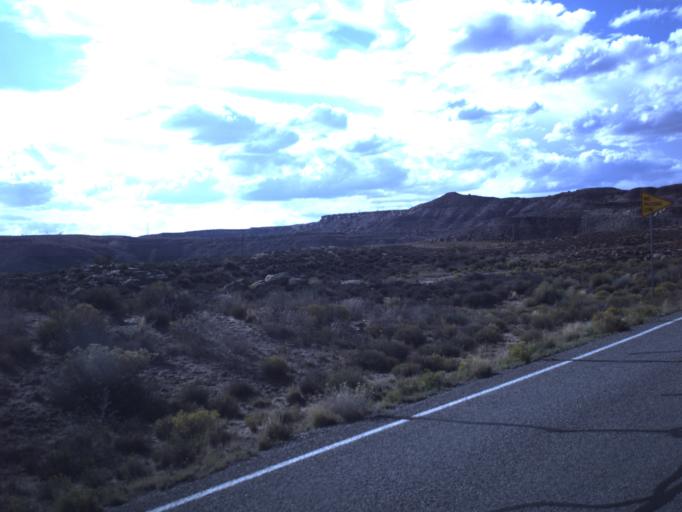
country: US
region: Utah
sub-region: San Juan County
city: Blanding
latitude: 37.3170
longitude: -109.3072
